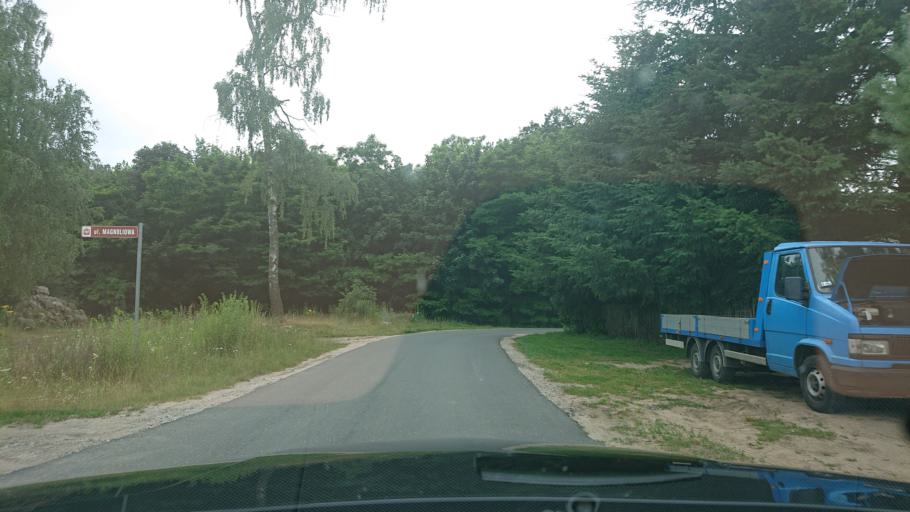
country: PL
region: Greater Poland Voivodeship
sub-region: Powiat gnieznienski
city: Gniezno
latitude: 52.5075
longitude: 17.6100
